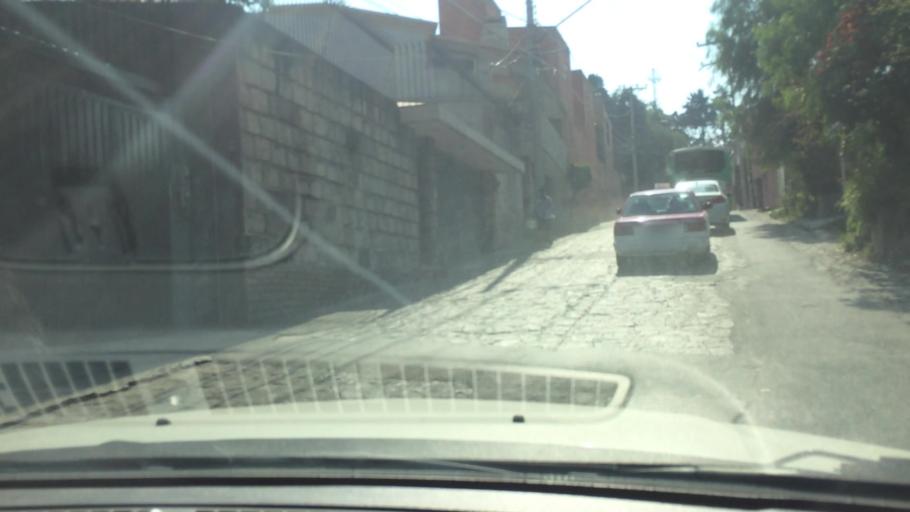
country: MX
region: Mexico City
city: Tlalpan
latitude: 19.2637
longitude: -99.1724
